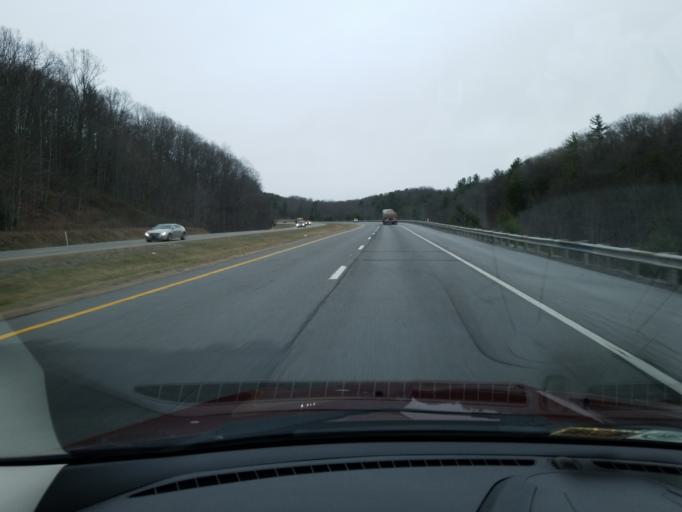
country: US
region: West Virginia
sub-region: Mercer County
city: Athens
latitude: 37.3466
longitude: -81.0136
